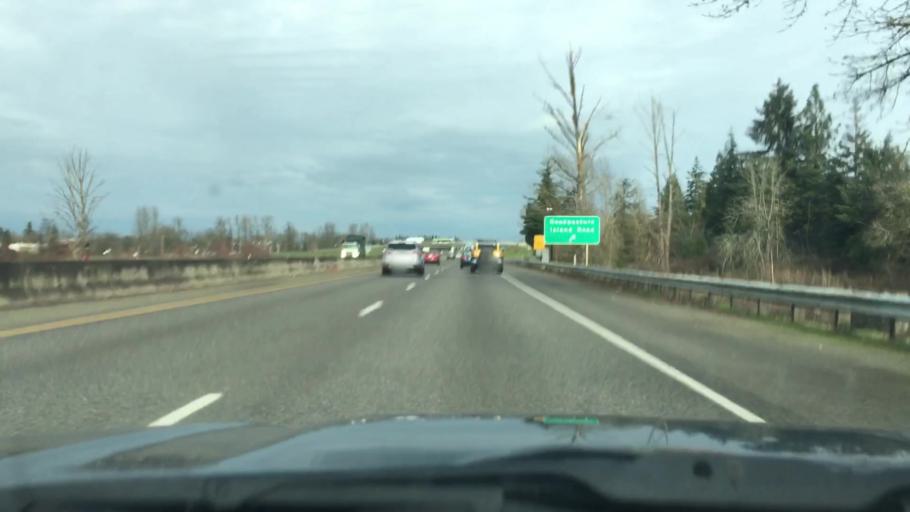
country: US
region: Oregon
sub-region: Lane County
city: Eugene
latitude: 44.0811
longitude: -123.1038
